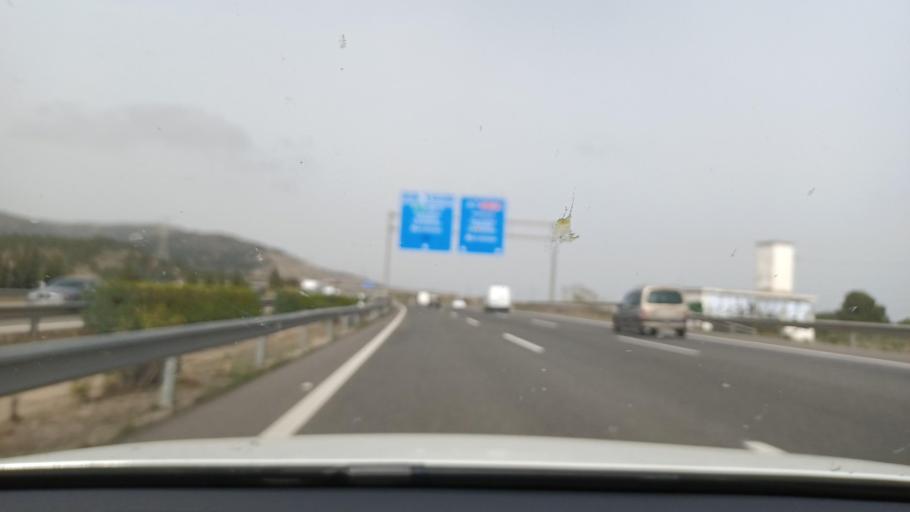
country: ES
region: Valencia
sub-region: Provincia de Valencia
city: Petres
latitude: 39.6874
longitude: -0.2876
